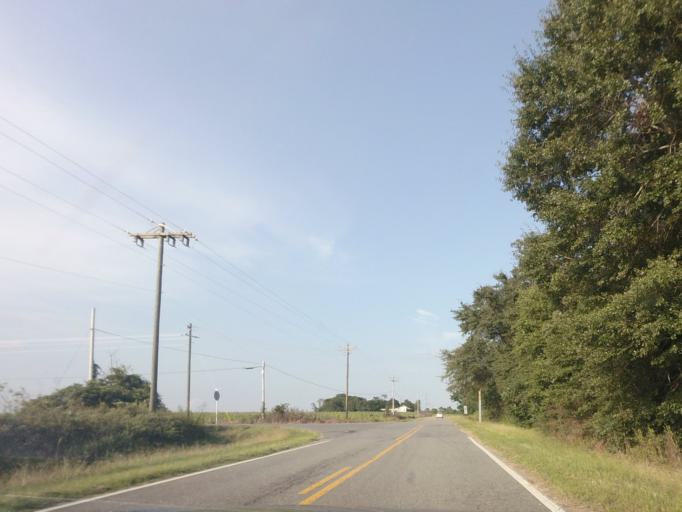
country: US
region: Georgia
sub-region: Bleckley County
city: Cochran
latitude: 32.4988
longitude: -83.2969
